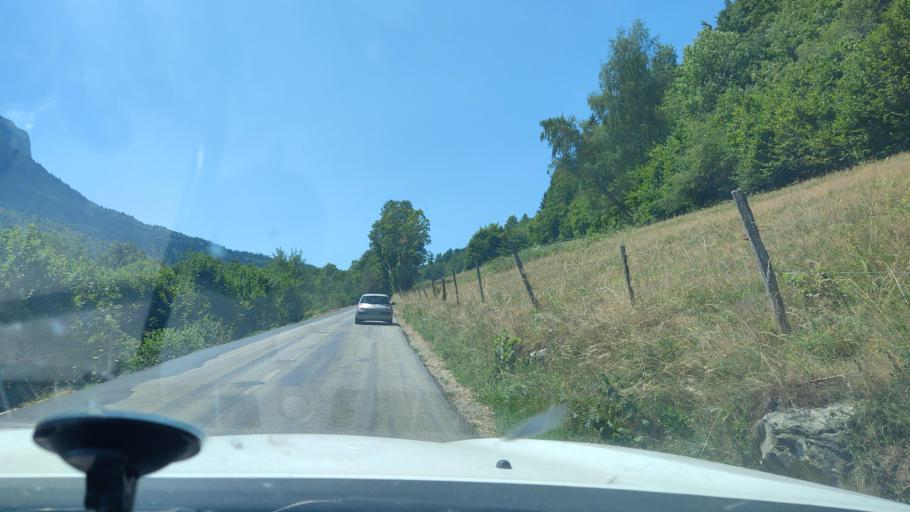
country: FR
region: Rhone-Alpes
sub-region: Departement de la Savoie
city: Mery
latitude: 45.6600
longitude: 6.0330
